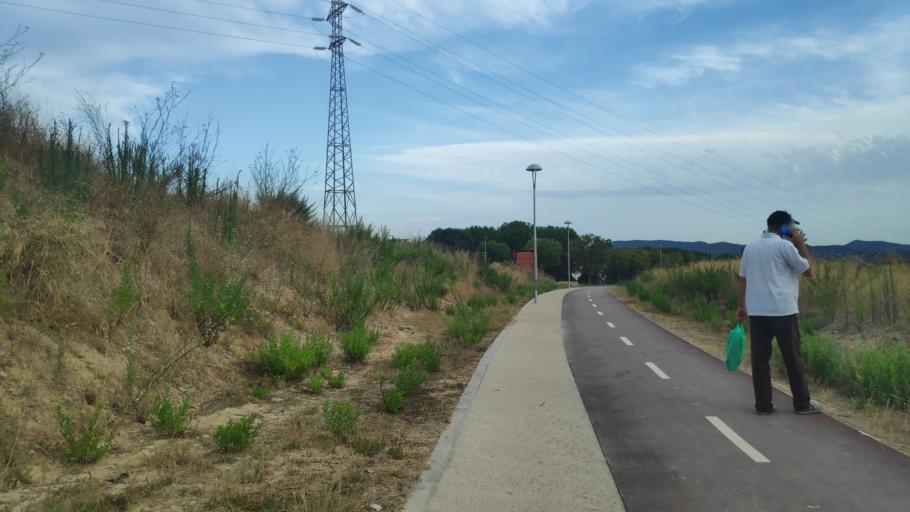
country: ES
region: Catalonia
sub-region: Provincia de Barcelona
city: Rubi
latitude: 41.4918
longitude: 2.0431
